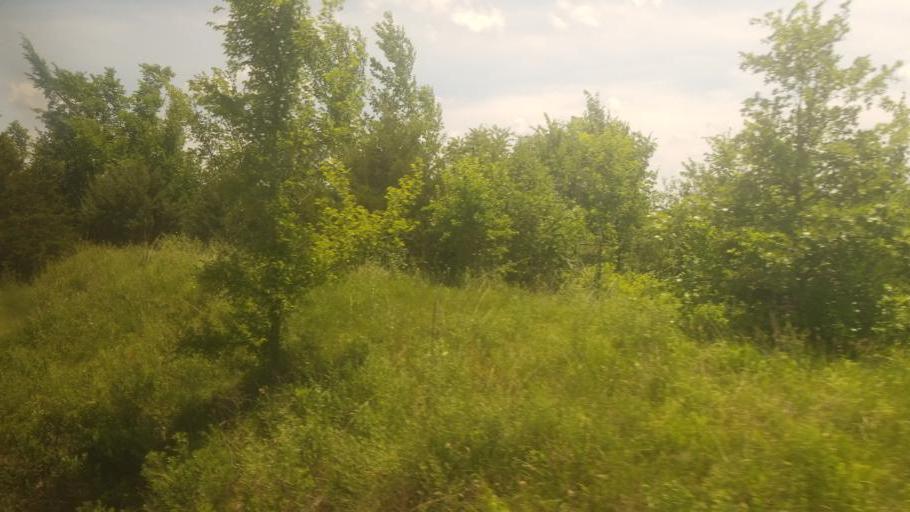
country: US
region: Missouri
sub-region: Linn County
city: Marceline
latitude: 39.8446
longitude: -92.8183
